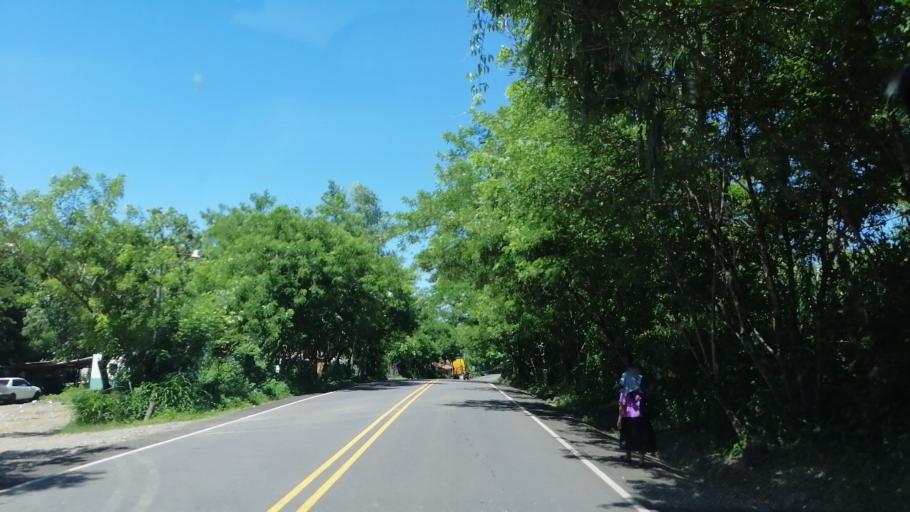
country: SV
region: Morazan
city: Cacaopera
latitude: 13.8084
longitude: -88.1598
